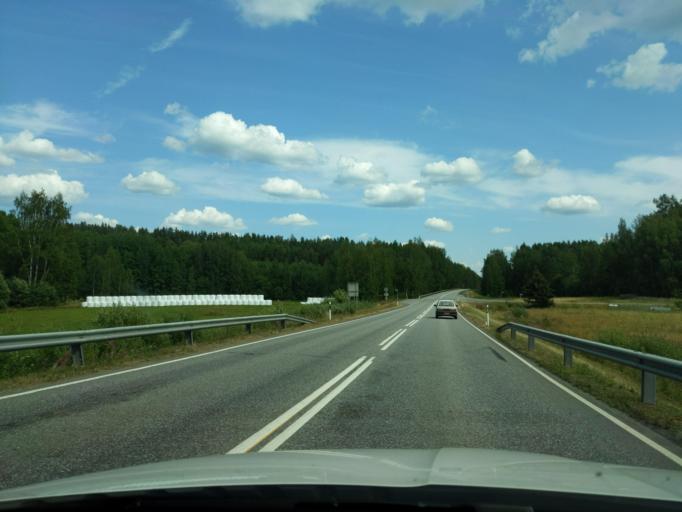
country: FI
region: Haeme
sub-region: Haemeenlinna
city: Lammi
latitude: 61.1291
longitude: 24.9646
